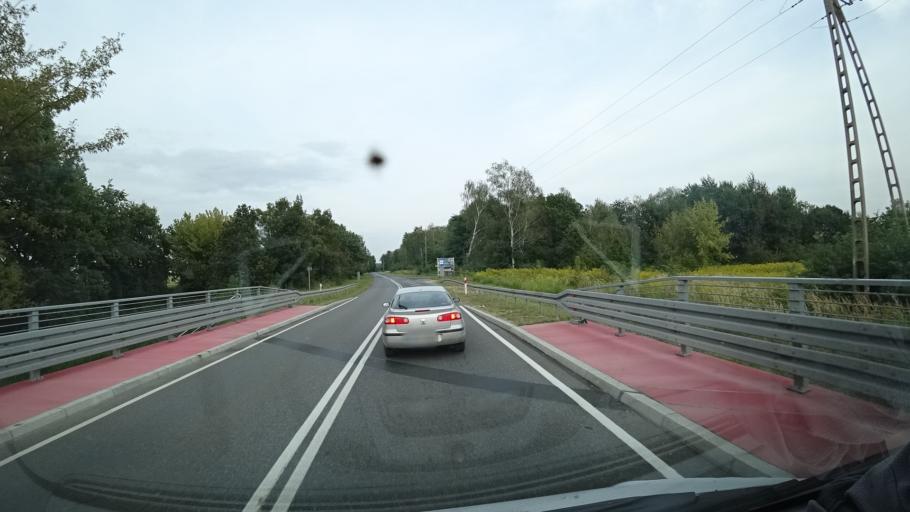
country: PL
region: Silesian Voivodeship
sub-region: Powiat gliwicki
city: Toszek
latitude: 50.3859
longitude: 18.5497
